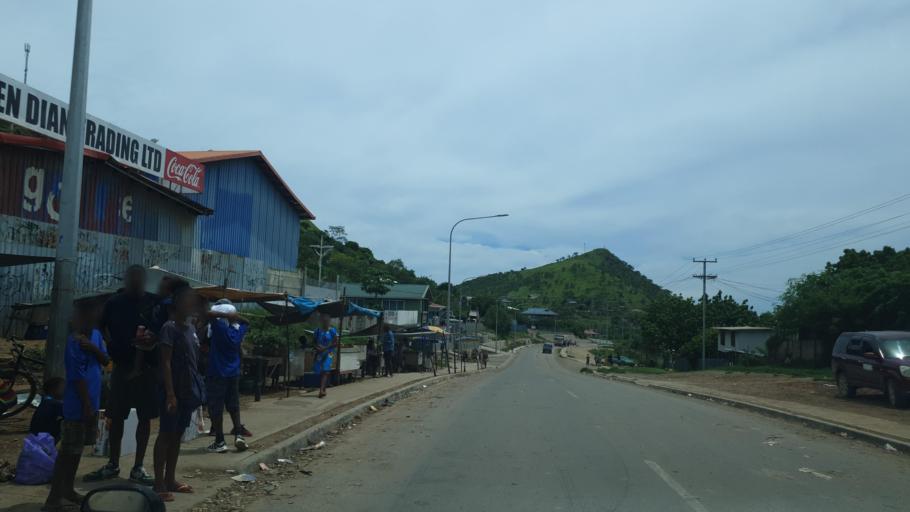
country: PG
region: National Capital
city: Port Moresby
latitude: -9.5205
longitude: 147.2411
